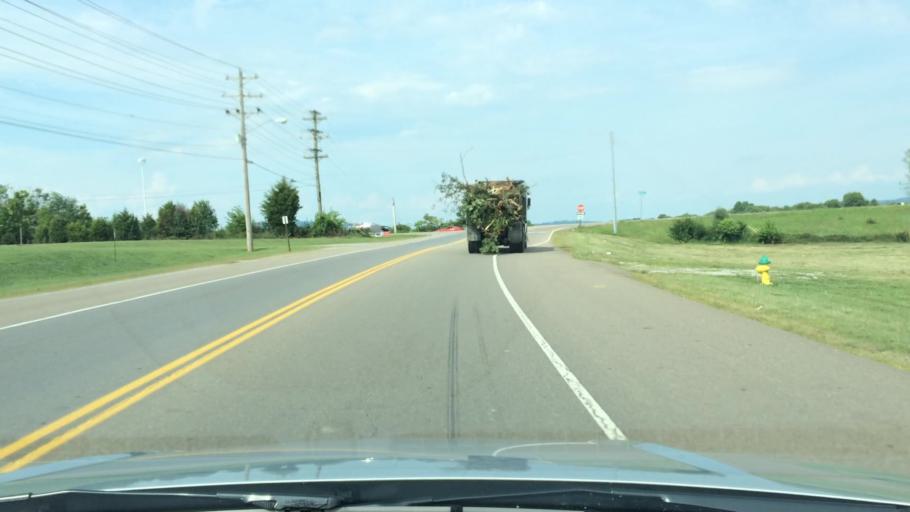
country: US
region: Tennessee
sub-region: Hamblen County
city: Morristown
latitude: 36.1719
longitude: -83.3886
